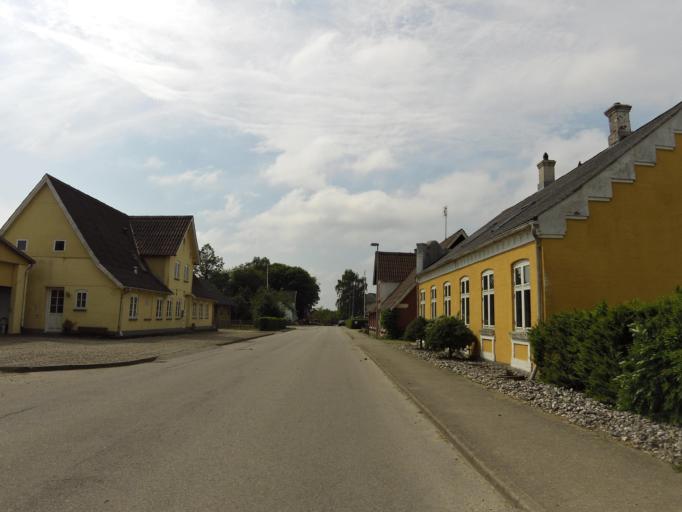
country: DK
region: South Denmark
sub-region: Haderslev Kommune
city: Vojens
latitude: 55.2691
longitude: 9.1885
